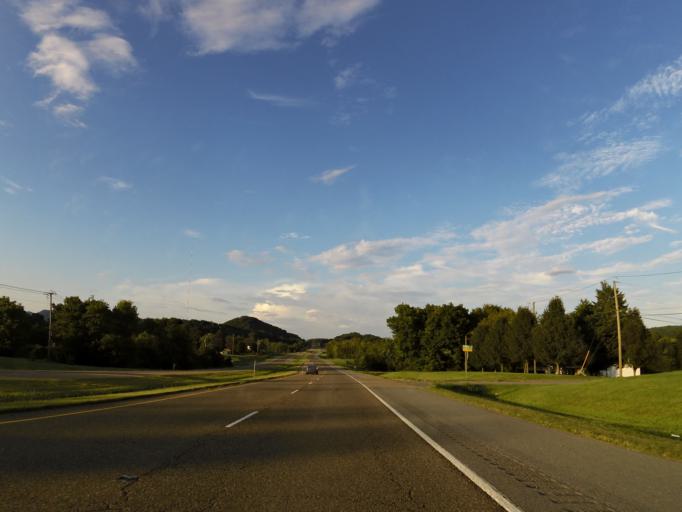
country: US
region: Tennessee
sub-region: Knox County
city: Mascot
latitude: 36.1084
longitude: -83.7377
